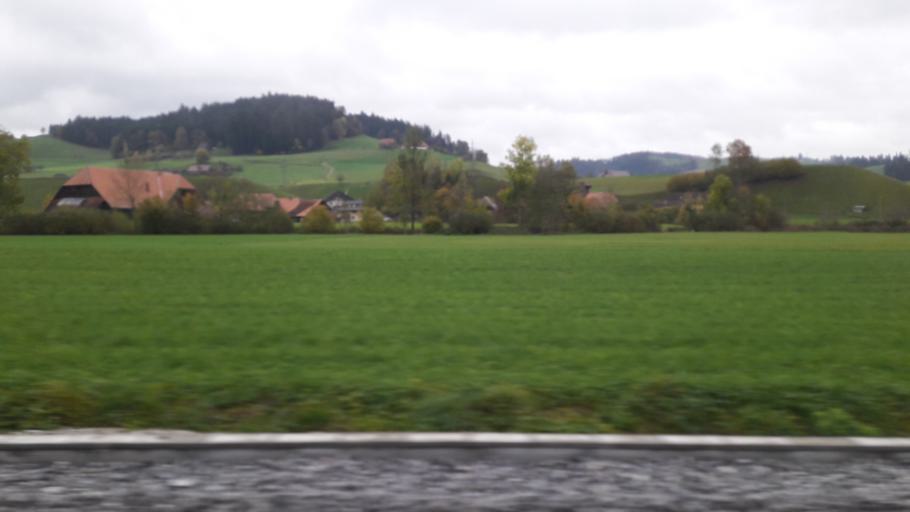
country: CH
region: Bern
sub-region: Emmental District
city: Trachselwald
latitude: 47.0107
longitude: 7.7244
